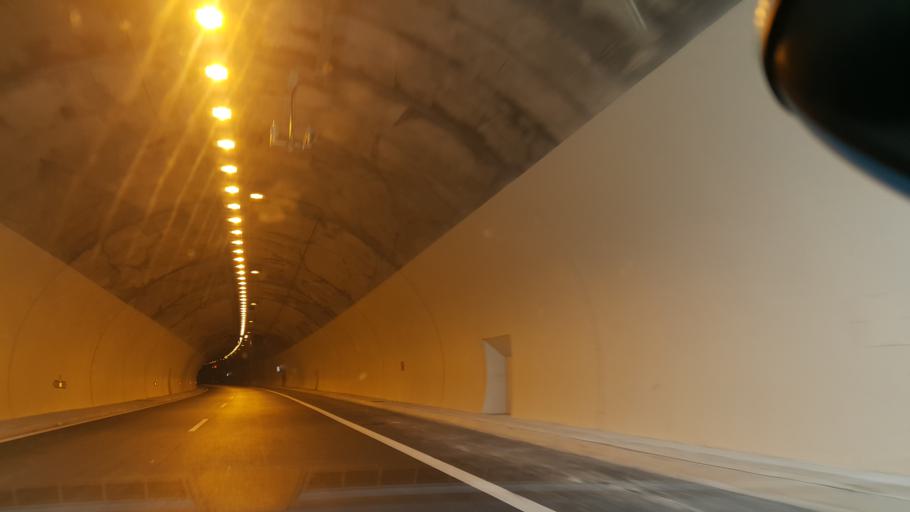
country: GR
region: Central Macedonia
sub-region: Nomos Pierias
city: Leptokarya
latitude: 40.0108
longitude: 22.5818
